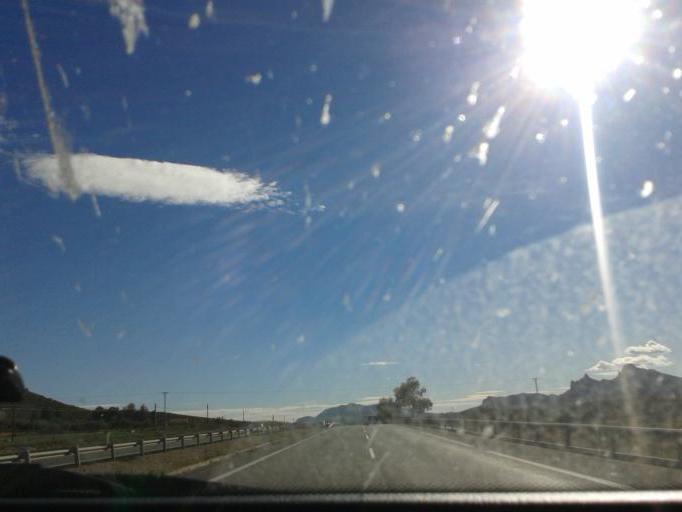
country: ES
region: Valencia
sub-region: Provincia de Alicante
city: Villena
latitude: 38.5907
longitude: -0.8444
